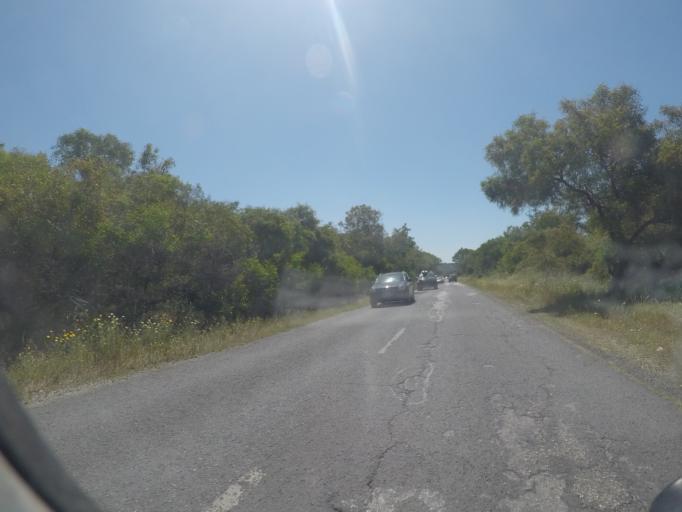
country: PT
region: Setubal
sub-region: Almada
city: Charneca
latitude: 38.6132
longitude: -9.2093
